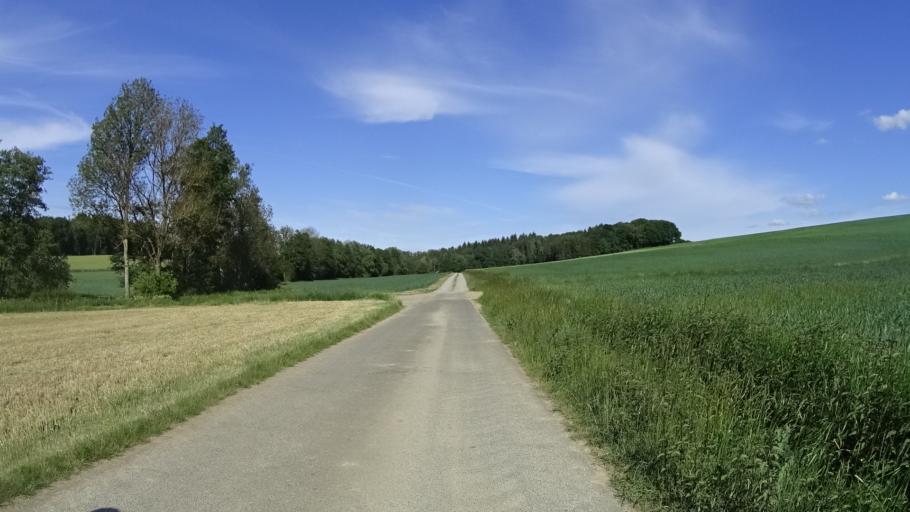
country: DE
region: Baden-Wuerttemberg
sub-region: Regierungsbezirk Stuttgart
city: Buch am Ahorn
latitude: 49.5259
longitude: 9.5325
